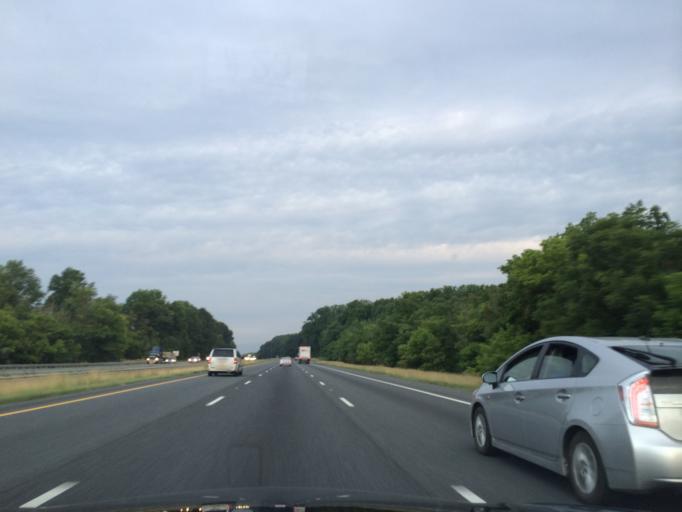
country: US
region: Maryland
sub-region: Carroll County
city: Mount Airy
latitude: 39.3435
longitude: -77.0737
